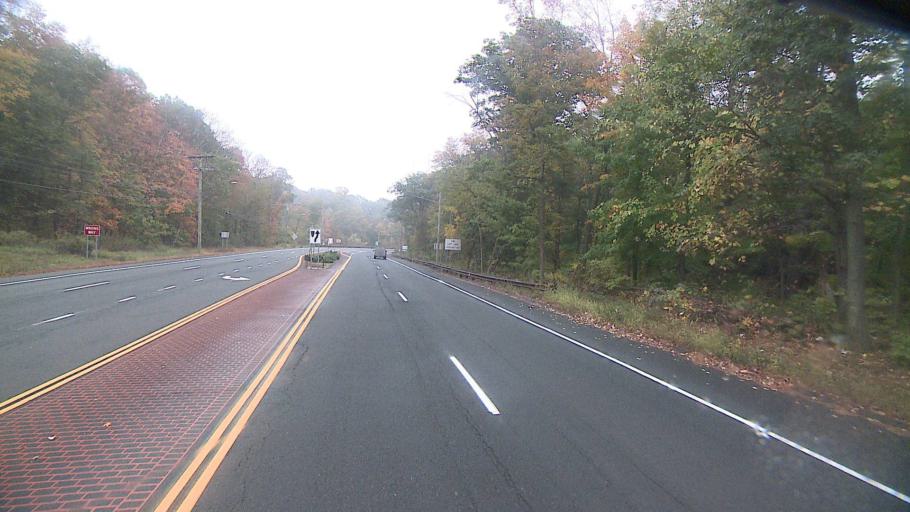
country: US
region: Connecticut
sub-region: Hartford County
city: Weatogue
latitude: 41.7977
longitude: -72.8011
